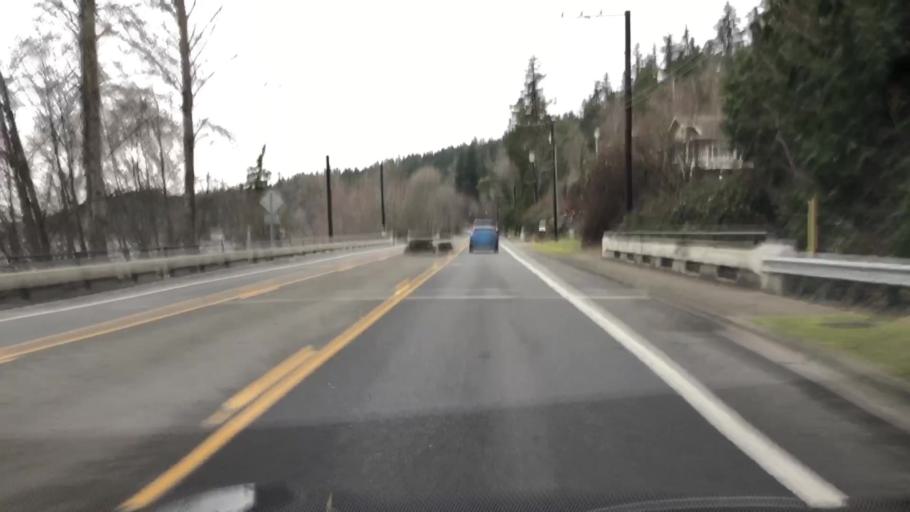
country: US
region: Washington
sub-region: King County
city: Sammamish
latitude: 47.6276
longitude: -122.0702
